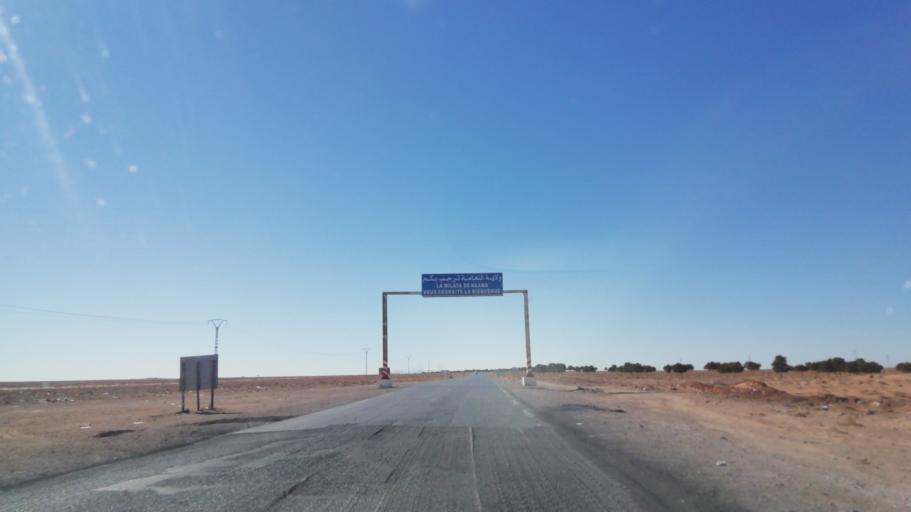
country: DZ
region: Saida
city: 'Ain el Hadjar
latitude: 34.0067
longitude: 0.0493
